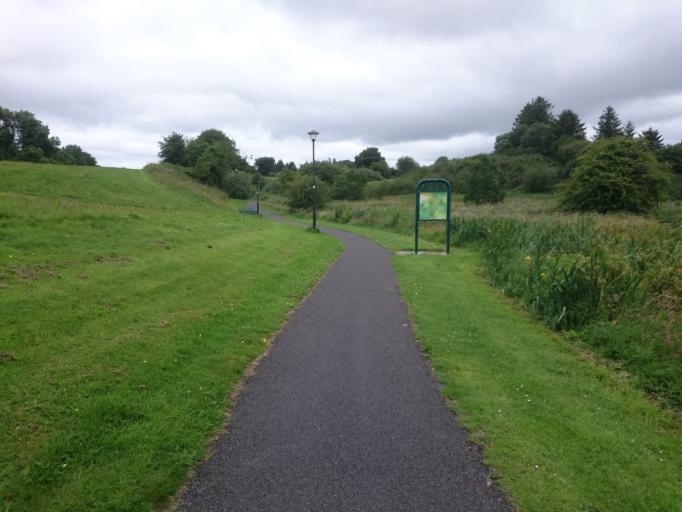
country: IE
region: Connaught
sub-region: Maigh Eo
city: Ballyhaunis
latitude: 53.7637
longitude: -8.7609
